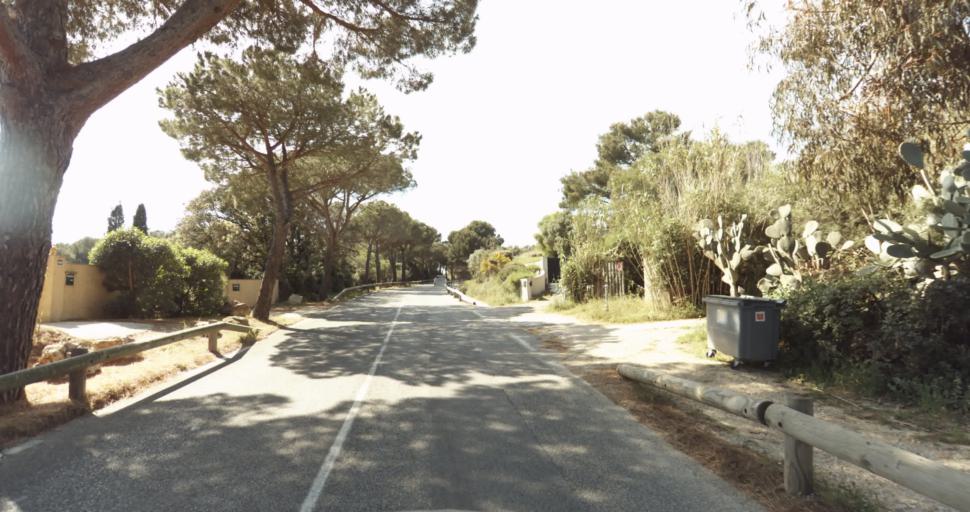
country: FR
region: Provence-Alpes-Cote d'Azur
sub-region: Departement du Var
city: Hyeres
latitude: 43.0317
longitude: 6.1514
